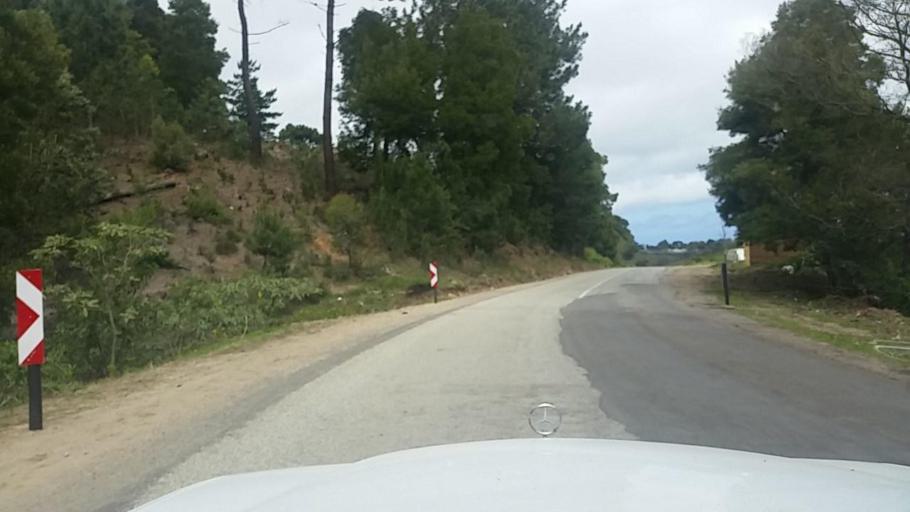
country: ZA
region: Western Cape
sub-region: Eden District Municipality
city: Knysna
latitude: -34.0287
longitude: 23.1105
